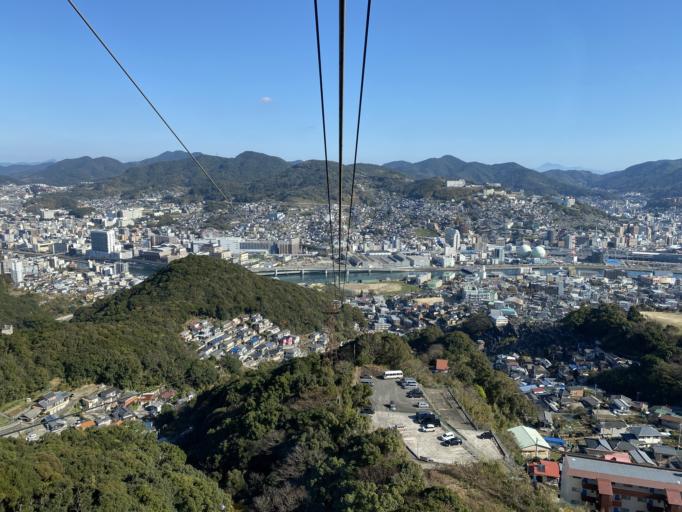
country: JP
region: Nagasaki
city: Nagasaki-shi
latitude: 32.7553
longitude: 129.8521
